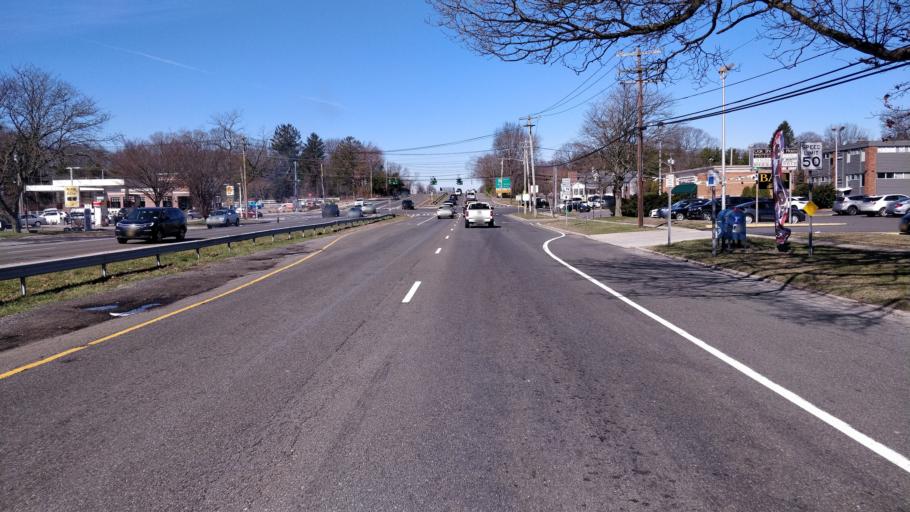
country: US
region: New York
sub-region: Suffolk County
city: Commack
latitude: 40.8385
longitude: -73.2777
